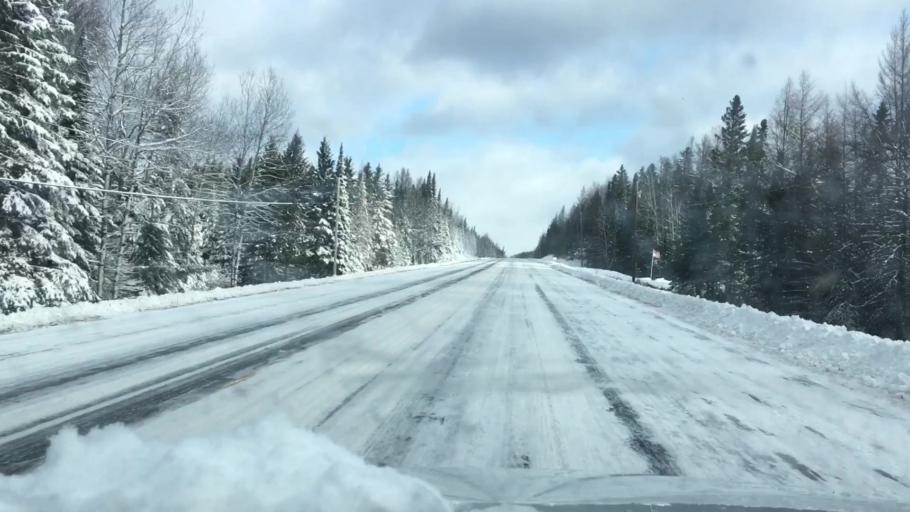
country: US
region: Maine
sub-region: Aroostook County
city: Madawaska
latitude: 47.0236
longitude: -68.0122
